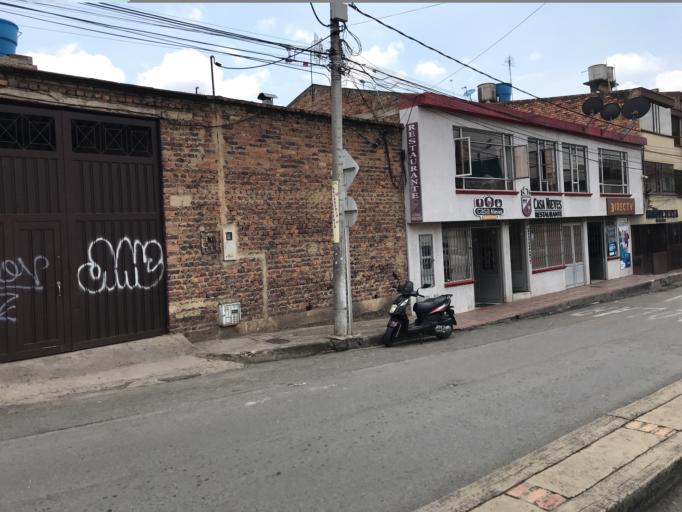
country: CO
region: Boyaca
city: Tunja
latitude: 5.5374
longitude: -73.3595
